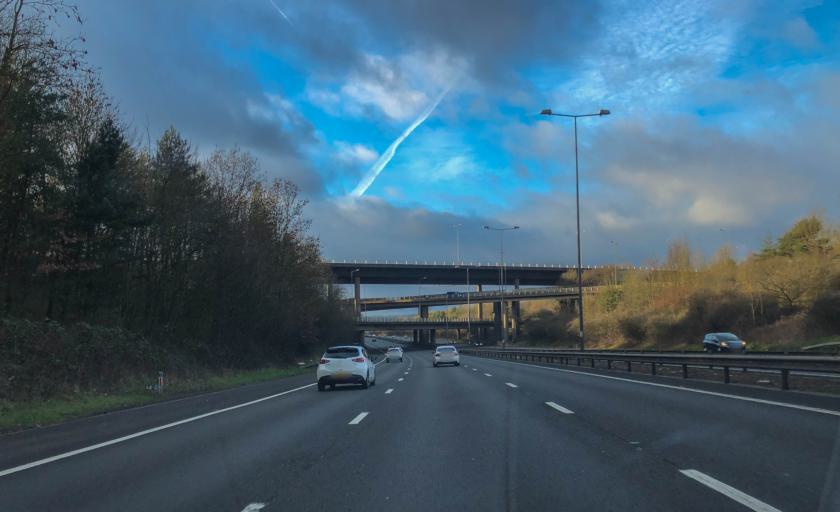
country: GB
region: England
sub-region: Surrey
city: Bletchingley
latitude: 51.2633
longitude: -0.1241
